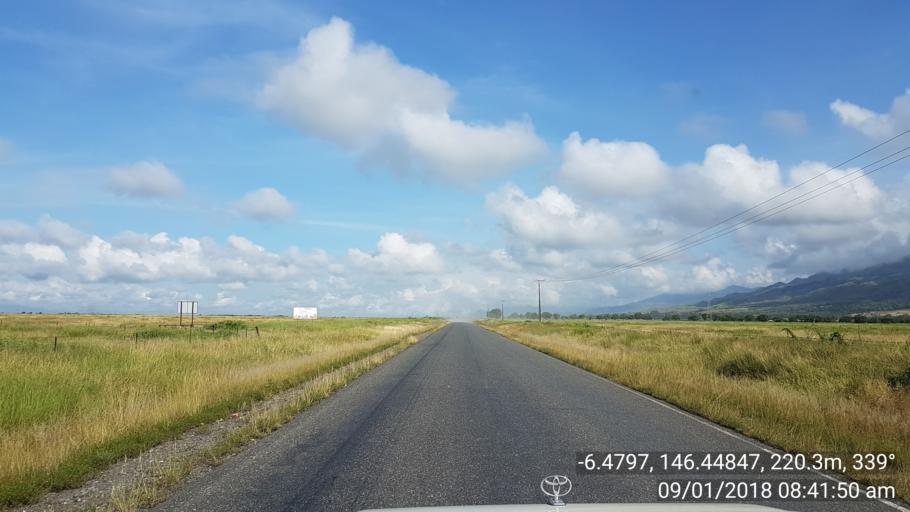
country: PG
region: Morobe
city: Lae
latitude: -6.4797
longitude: 146.4485
